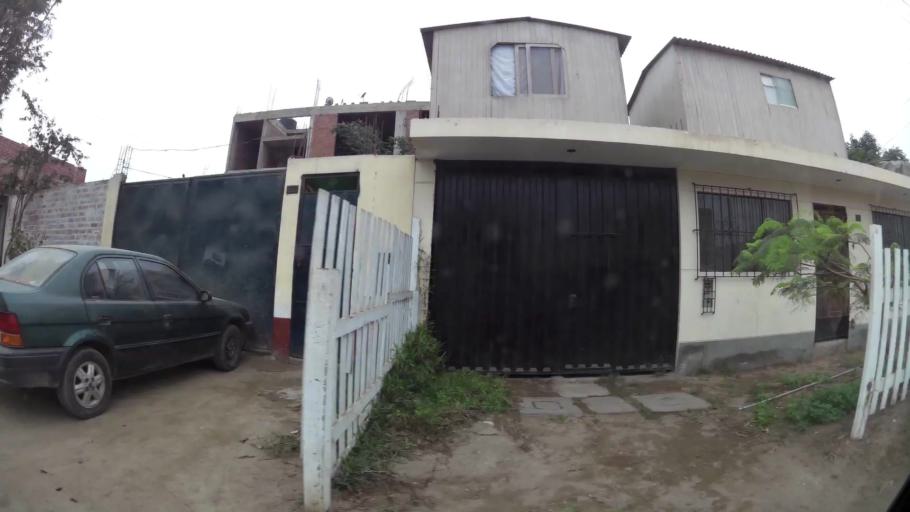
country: PE
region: Lima
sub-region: Lima
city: Surco
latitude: -12.2013
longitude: -76.9827
